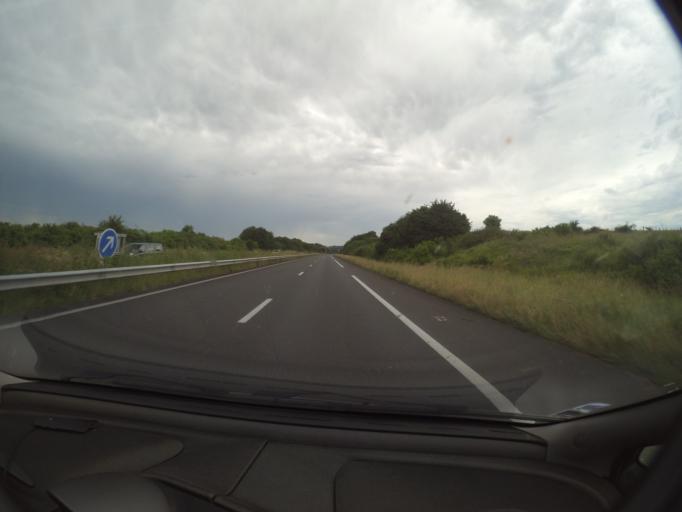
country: FR
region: Pays de la Loire
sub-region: Departement de la Sarthe
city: Louplande
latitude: 47.9374
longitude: -0.0437
